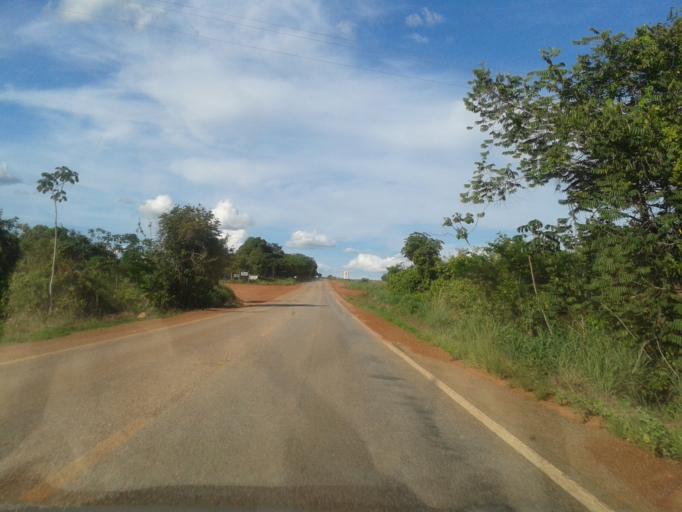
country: BR
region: Goias
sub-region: Mozarlandia
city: Mozarlandia
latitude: -14.4008
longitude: -50.4427
